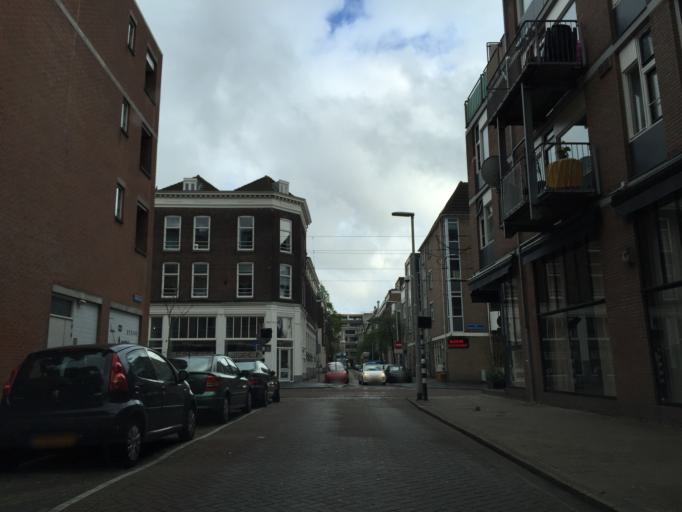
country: NL
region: South Holland
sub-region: Gemeente Rotterdam
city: Rotterdam
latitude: 51.9194
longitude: 4.4739
